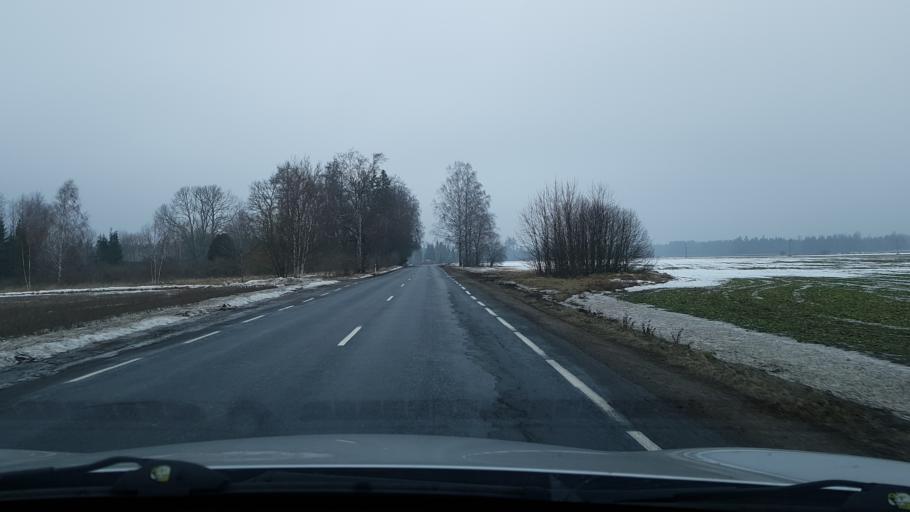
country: EE
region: Valgamaa
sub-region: Torva linn
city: Torva
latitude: 58.1572
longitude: 25.9634
